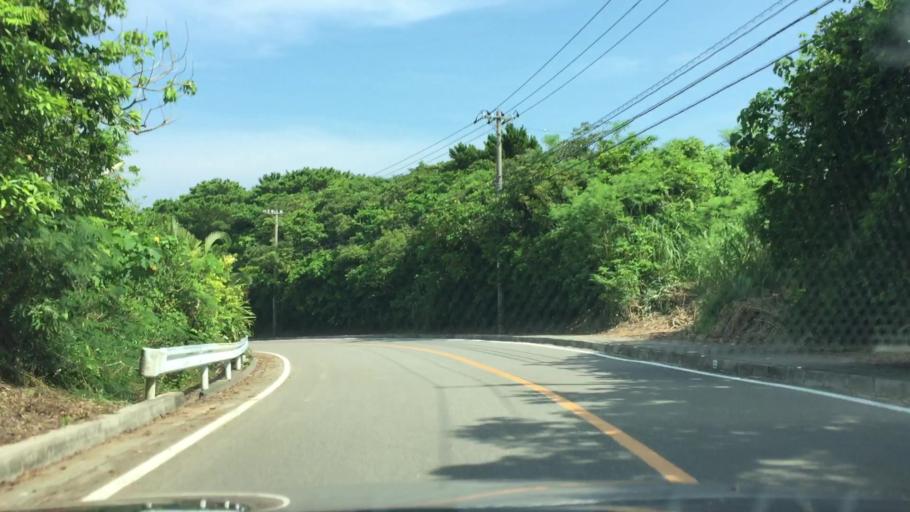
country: JP
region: Okinawa
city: Ishigaki
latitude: 24.5101
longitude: 124.2679
